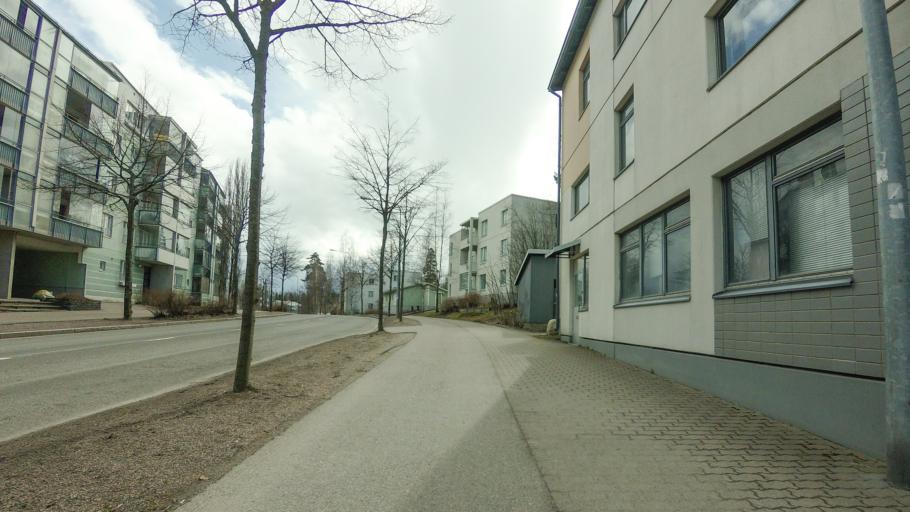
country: FI
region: Uusimaa
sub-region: Helsinki
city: Vantaa
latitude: 60.2037
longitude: 25.1171
